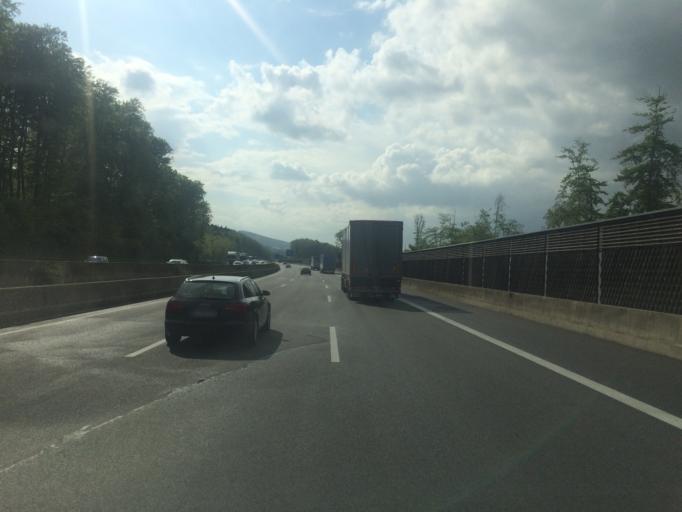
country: DE
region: Lower Saxony
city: Buchholz
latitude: 52.2194
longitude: 9.1504
